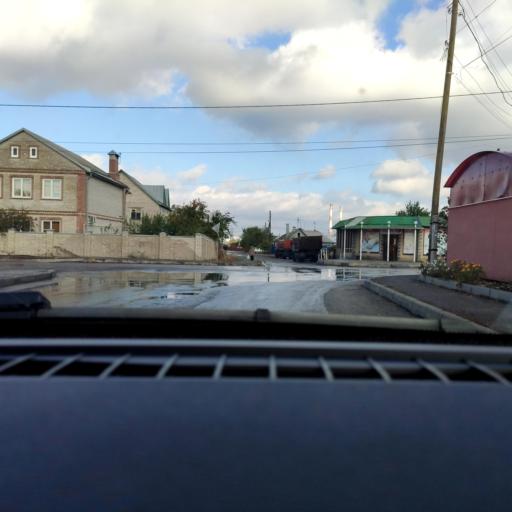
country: RU
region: Voronezj
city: Maslovka
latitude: 51.6100
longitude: 39.2207
